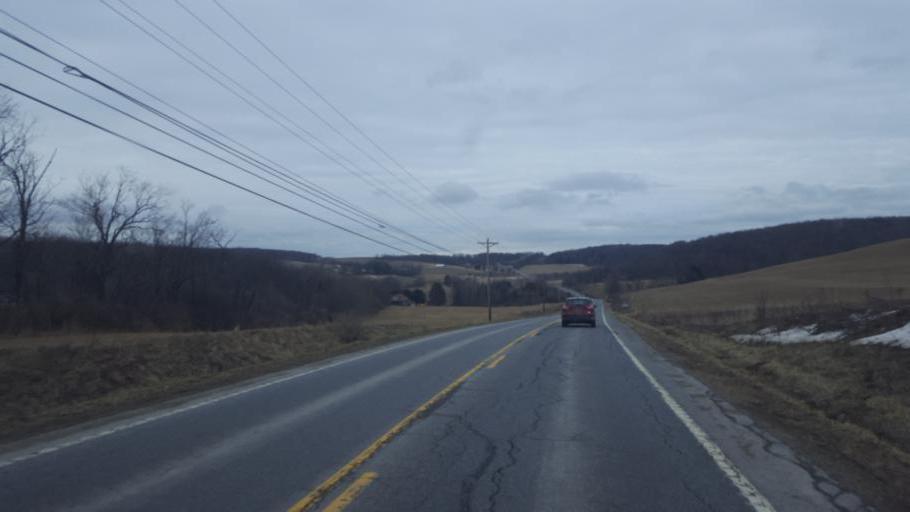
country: US
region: Pennsylvania
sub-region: Potter County
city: Galeton
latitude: 41.8856
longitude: -77.8048
